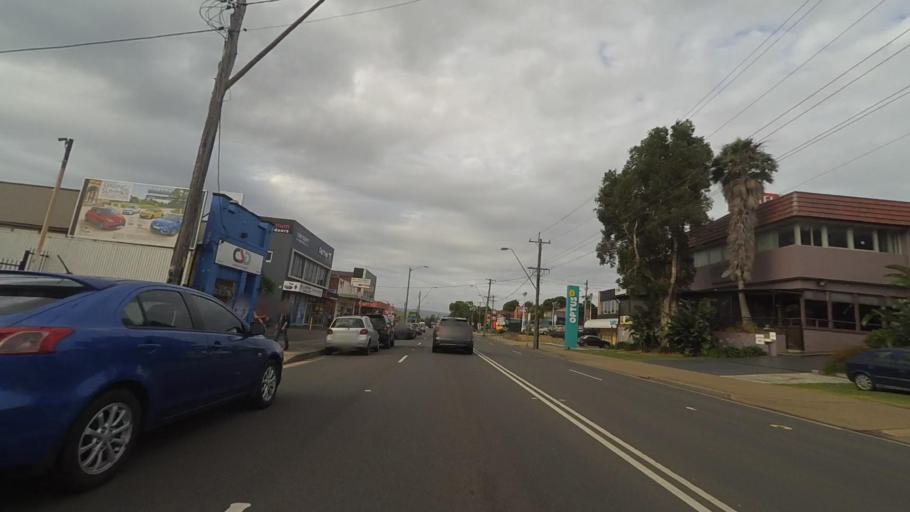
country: AU
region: New South Wales
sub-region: Wollongong
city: Gwynneville
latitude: -34.4164
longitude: 150.8926
